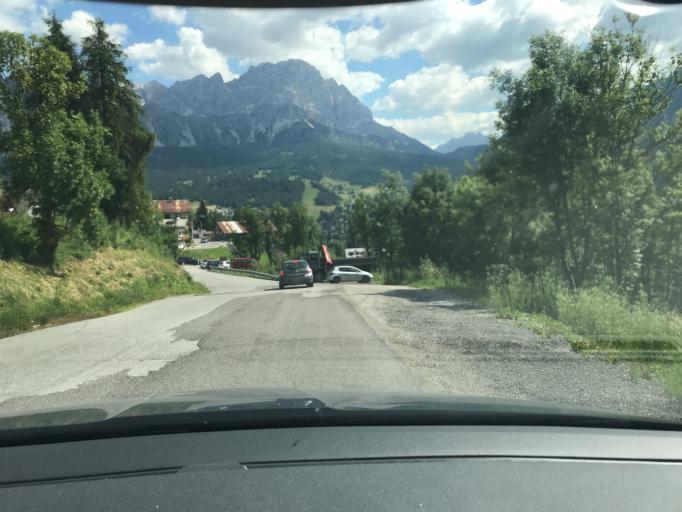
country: IT
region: Veneto
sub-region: Provincia di Belluno
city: Cortina d'Ampezzo
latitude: 46.5327
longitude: 12.1212
